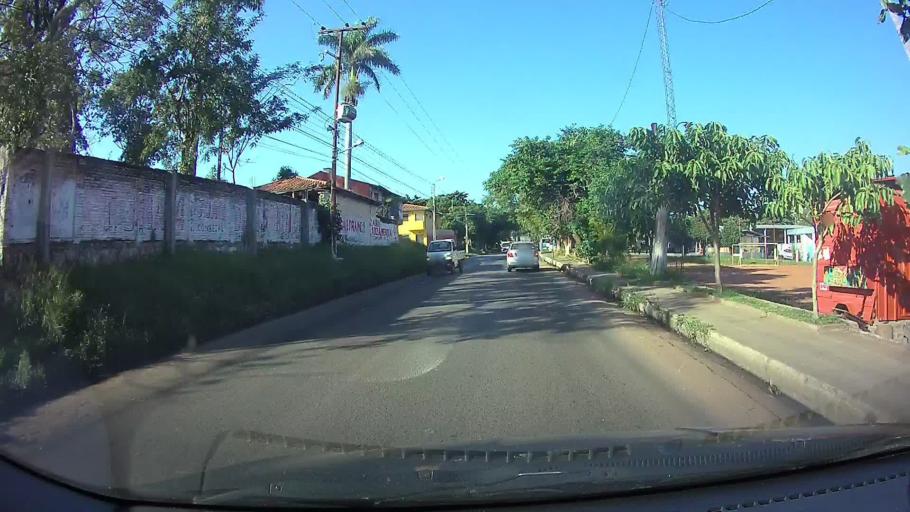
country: PY
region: Central
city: Lambare
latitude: -25.3484
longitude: -57.6011
